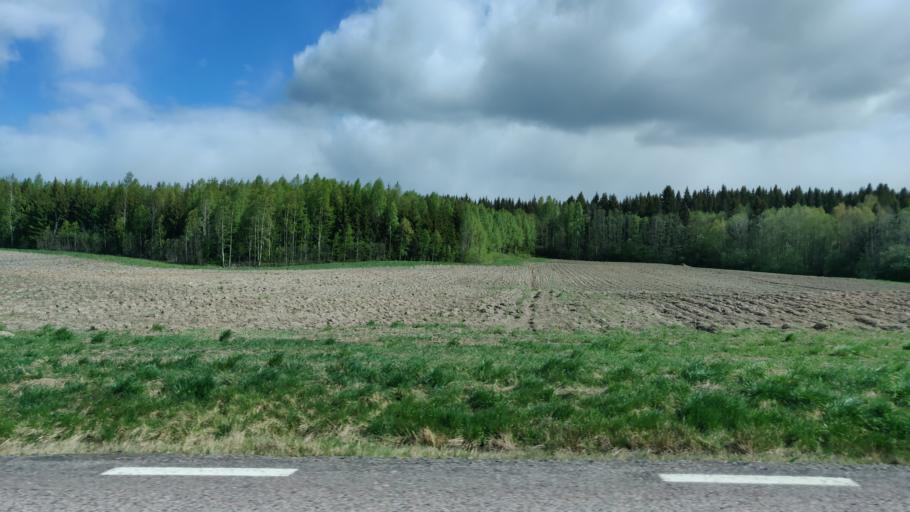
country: SE
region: Vaermland
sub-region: Karlstads Kommun
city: Molkom
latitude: 59.6391
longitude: 13.7168
